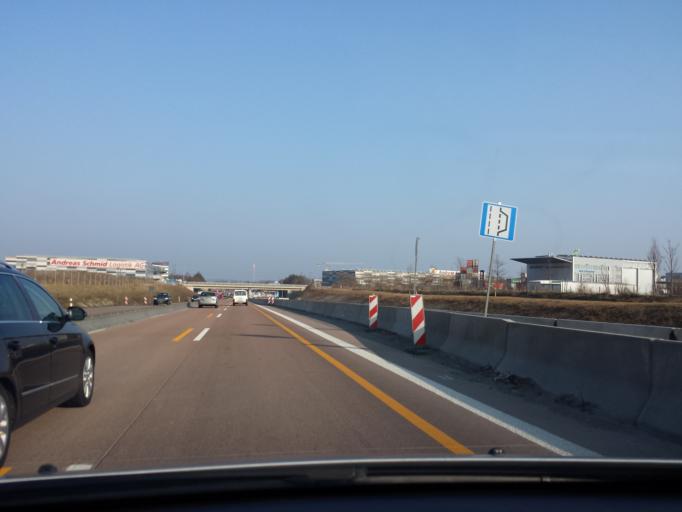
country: DE
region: Bavaria
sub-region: Swabia
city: Gersthofen
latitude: 48.4155
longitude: 10.8586
